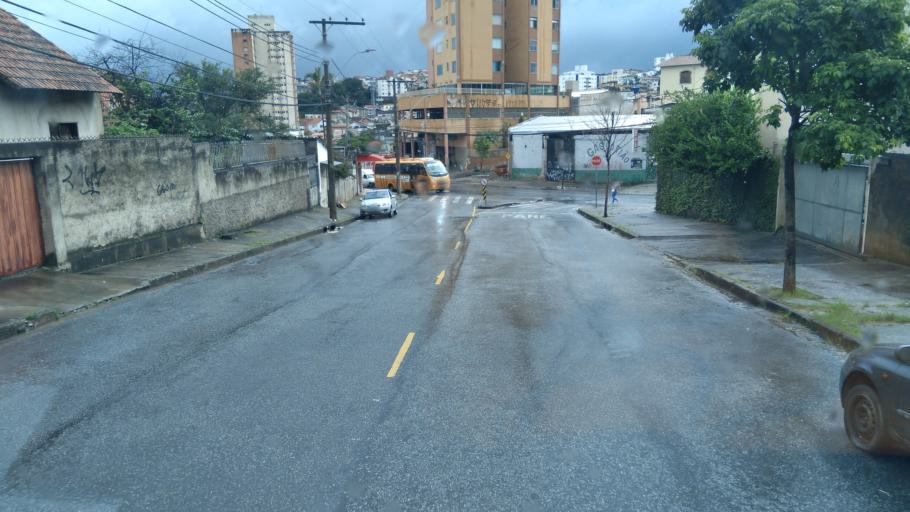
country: BR
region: Minas Gerais
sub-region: Belo Horizonte
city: Belo Horizonte
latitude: -19.9276
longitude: -43.9094
